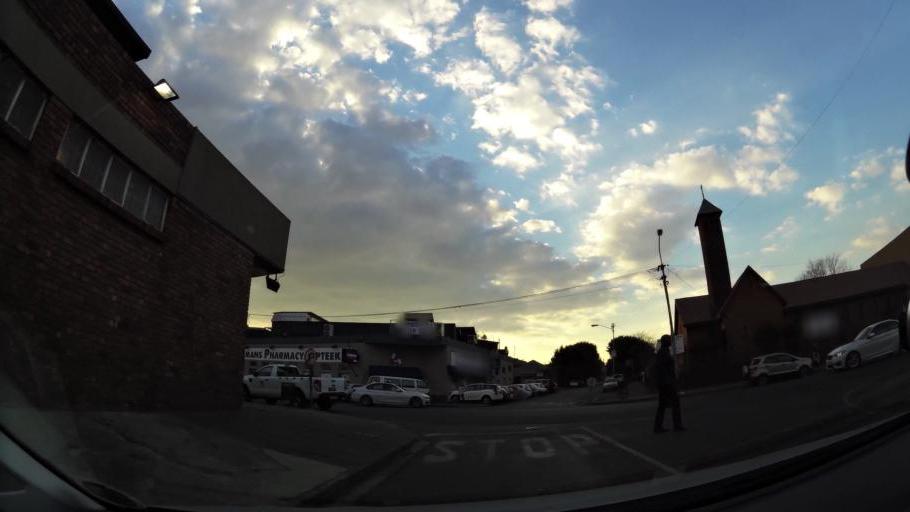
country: ZA
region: Gauteng
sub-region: Ekurhuleni Metropolitan Municipality
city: Germiston
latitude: -26.1901
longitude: 28.1577
